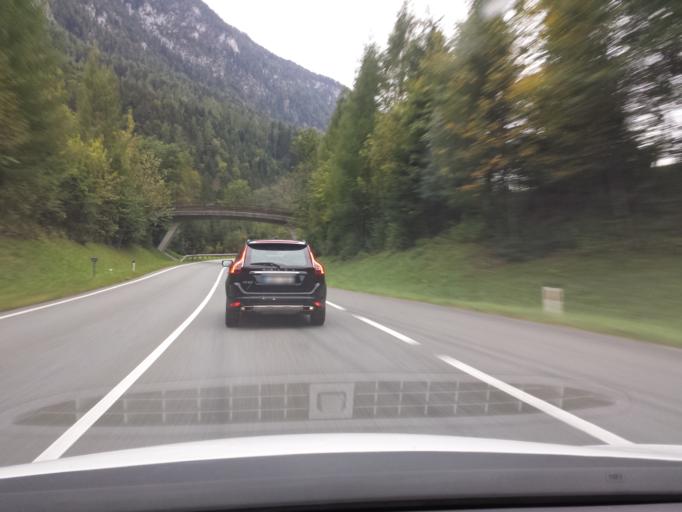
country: AT
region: Salzburg
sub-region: Politischer Bezirk Zell am See
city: Unken
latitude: 47.6619
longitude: 12.7463
